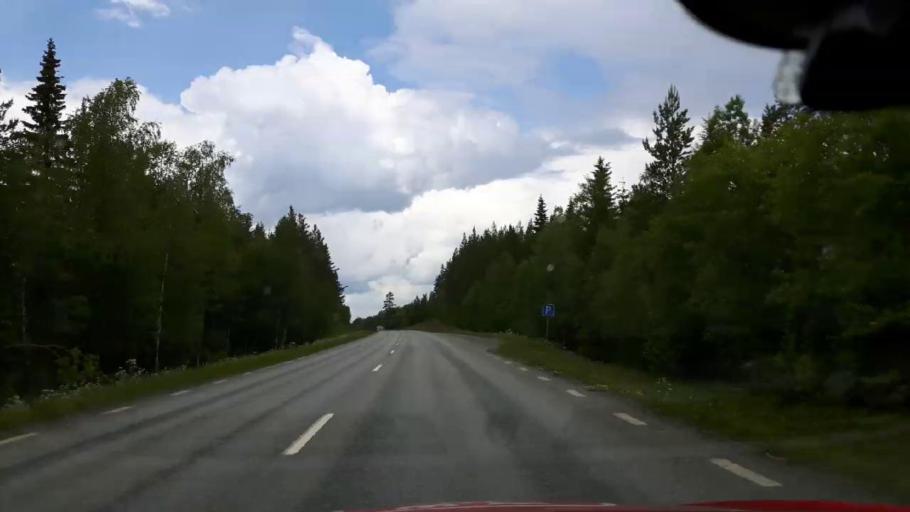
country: SE
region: Jaemtland
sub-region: Krokoms Kommun
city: Krokom
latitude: 63.3540
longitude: 14.4240
